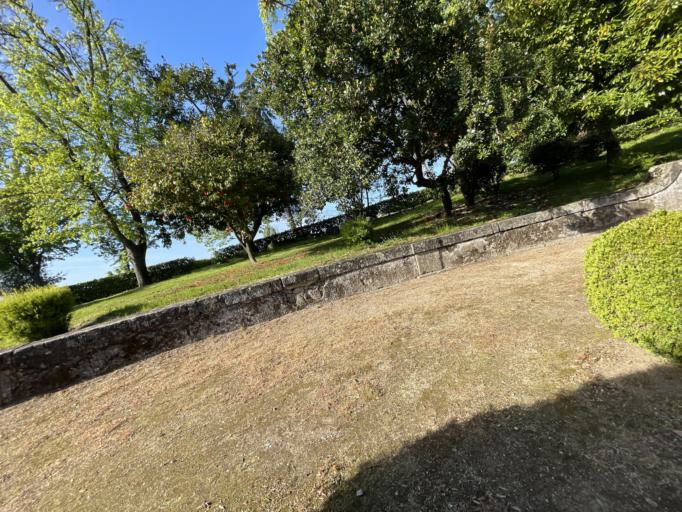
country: PT
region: Braga
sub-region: Guimaraes
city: Guimaraes
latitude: 41.4434
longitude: -8.2759
